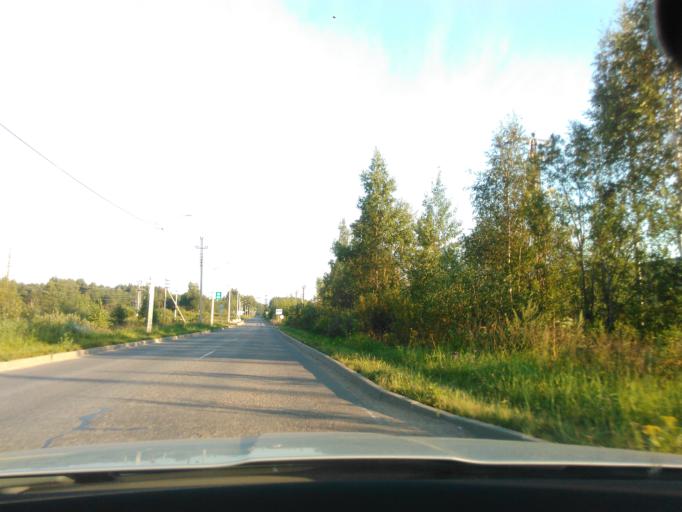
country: RU
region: Tverskaya
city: Konakovo
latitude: 56.7393
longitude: 36.7800
